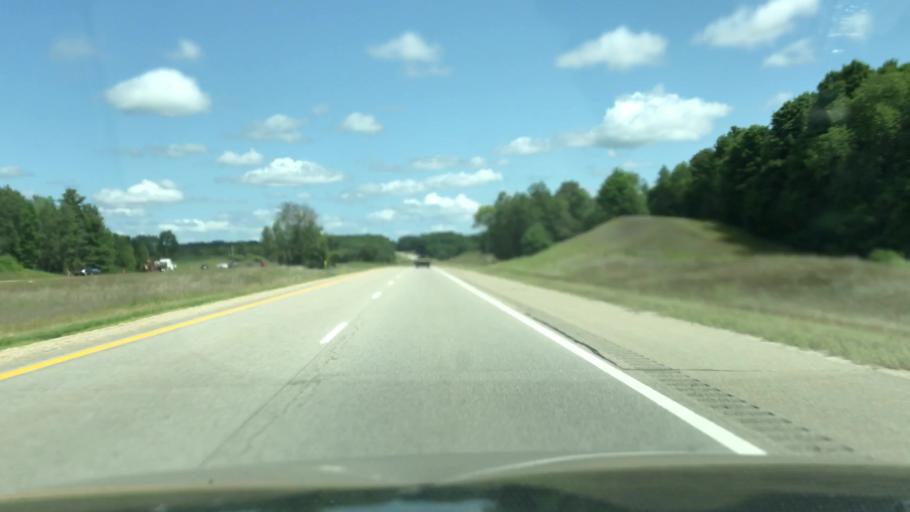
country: US
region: Michigan
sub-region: Osceola County
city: Reed City
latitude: 43.7957
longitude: -85.5337
